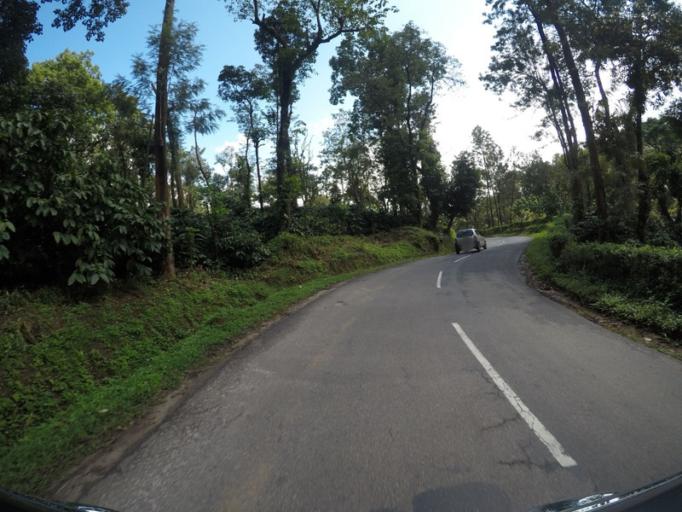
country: IN
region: Karnataka
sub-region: Kodagu
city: Suntikoppa
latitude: 12.4789
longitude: 75.7904
